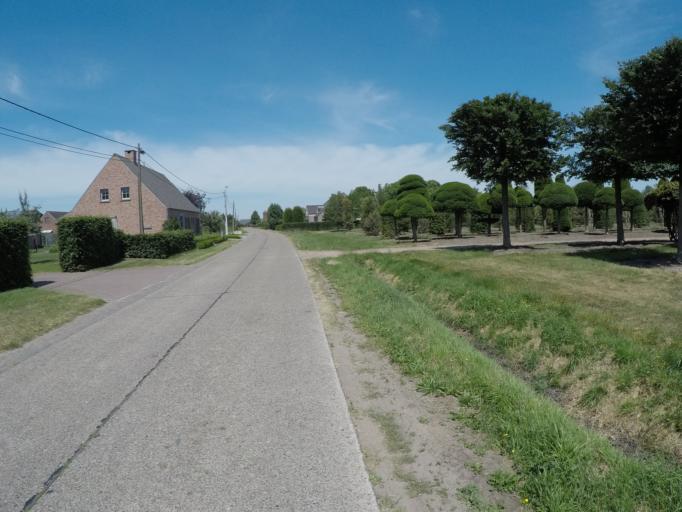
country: BE
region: Flanders
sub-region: Provincie Antwerpen
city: Wuustwezel
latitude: 51.3899
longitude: 4.6331
